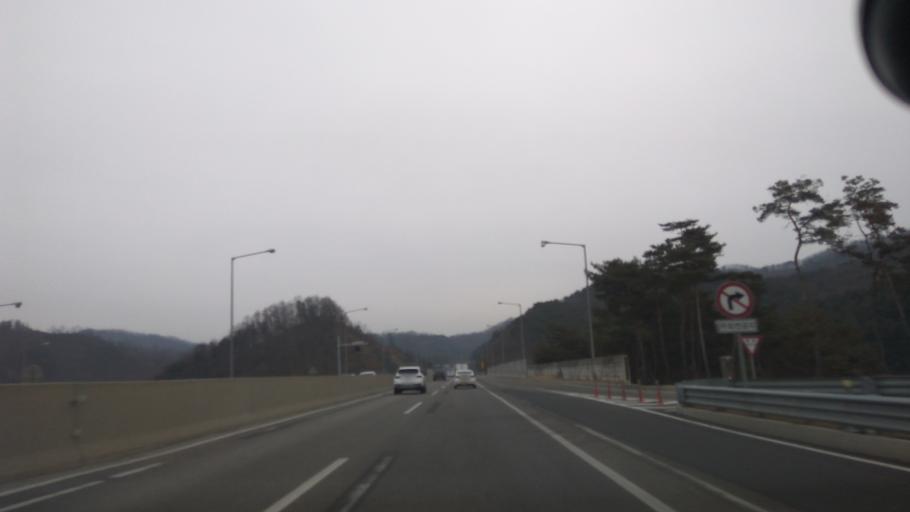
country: KR
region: Gangwon-do
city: Sindong
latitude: 37.7340
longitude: 127.6231
